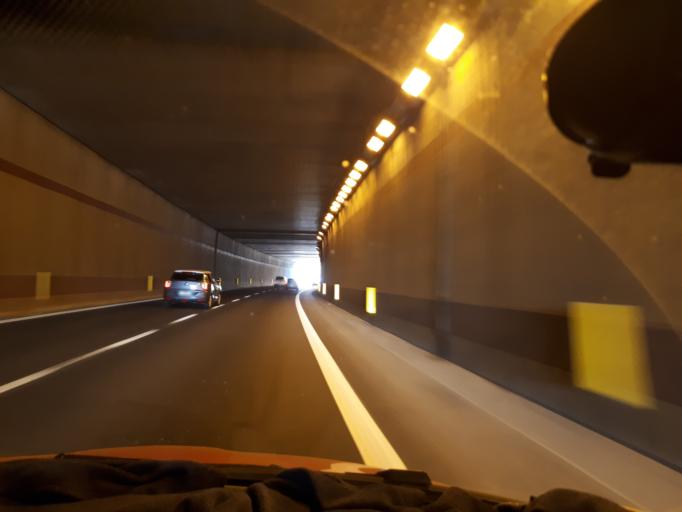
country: IT
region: Lombardy
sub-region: Provincia di Monza e Brianza
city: Lentate sul Seveso
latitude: 45.6735
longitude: 9.1122
